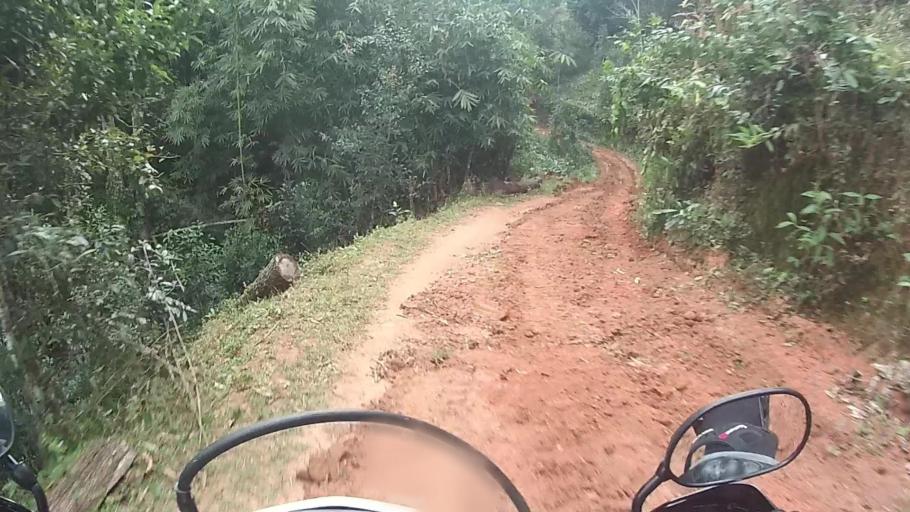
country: TH
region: Chiang Mai
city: Mae On
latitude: 18.7954
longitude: 99.3444
